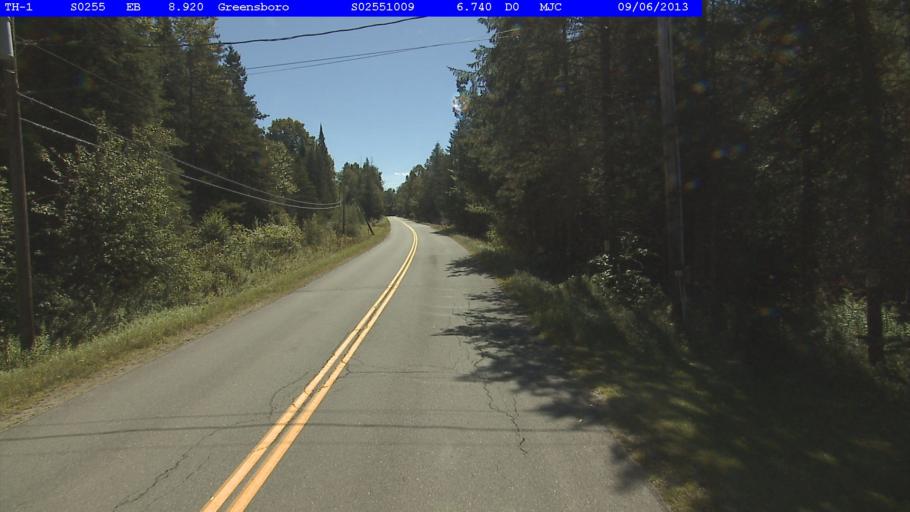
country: US
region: Vermont
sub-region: Caledonia County
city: Hardwick
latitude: 44.5571
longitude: -72.2769
